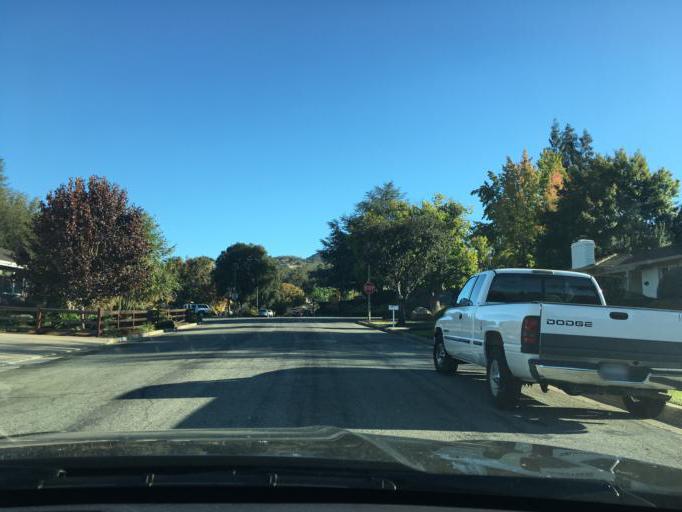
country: US
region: California
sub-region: Santa Clara County
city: Cambrian Park
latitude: 37.2110
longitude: -121.8731
